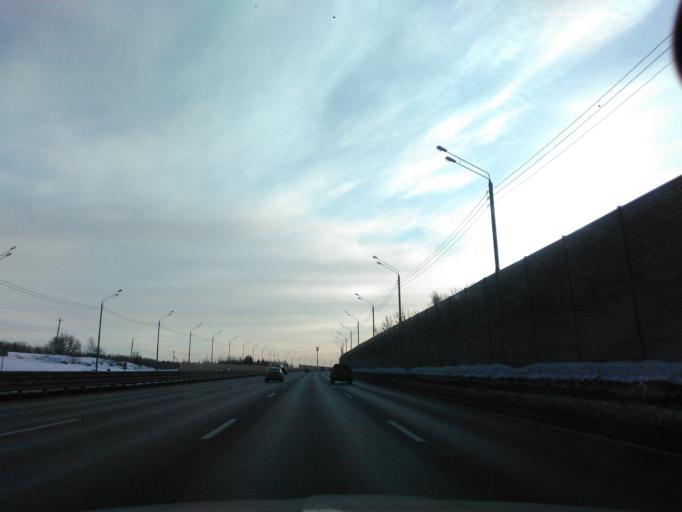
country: RU
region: Moskovskaya
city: Rozhdestveno
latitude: 55.8189
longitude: 37.0028
